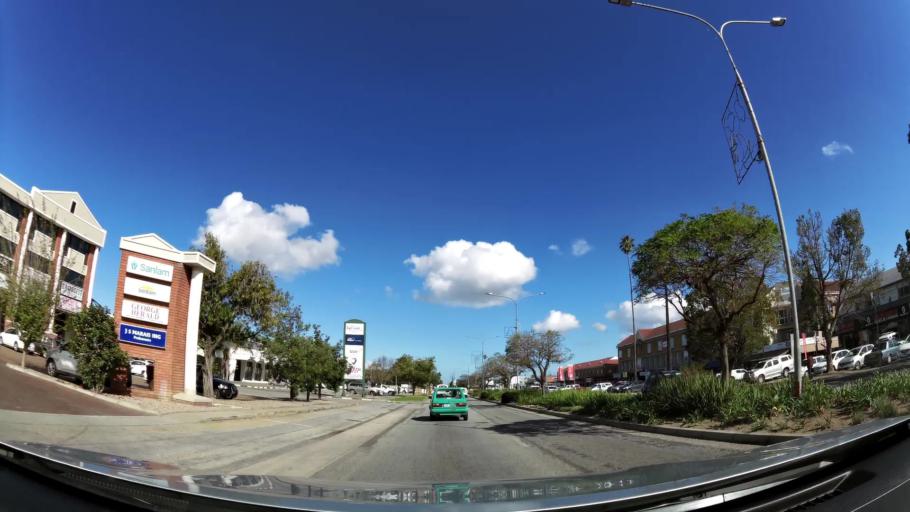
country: ZA
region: Western Cape
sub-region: Eden District Municipality
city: George
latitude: -33.9626
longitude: 22.4538
